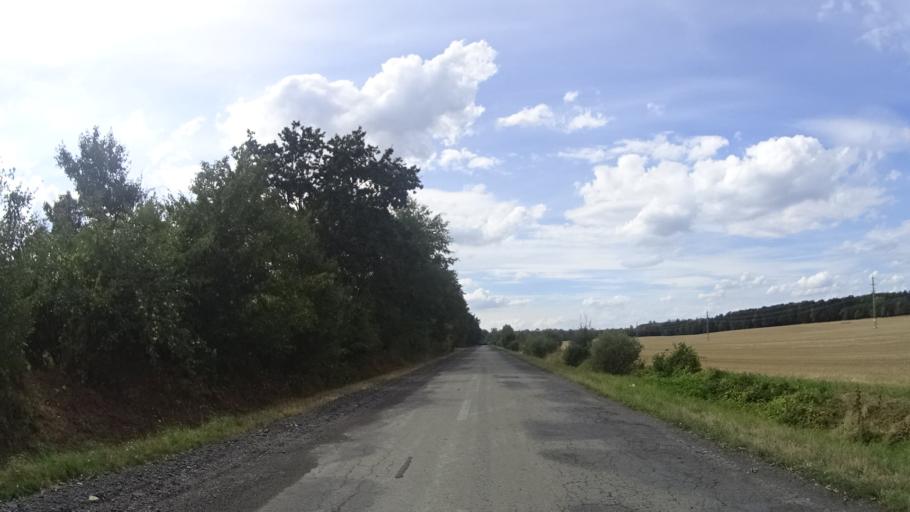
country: CZ
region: Olomoucky
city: Cervenka
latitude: 49.7169
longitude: 17.0452
